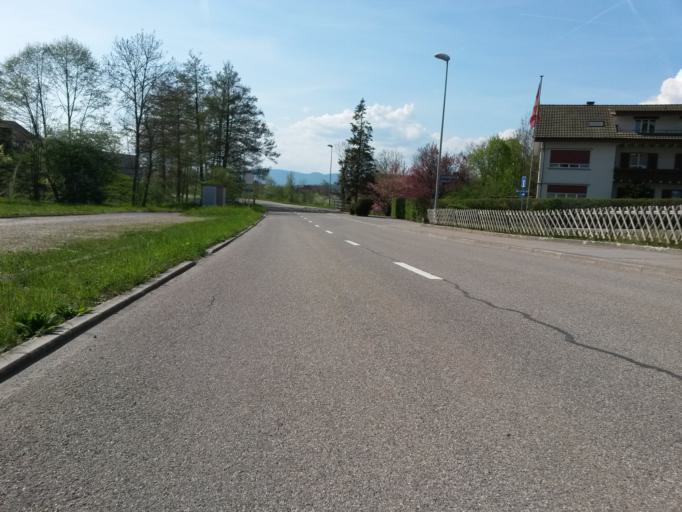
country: CH
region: Bern
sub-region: Oberaargau
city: Roggwil
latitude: 47.2333
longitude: 7.8404
